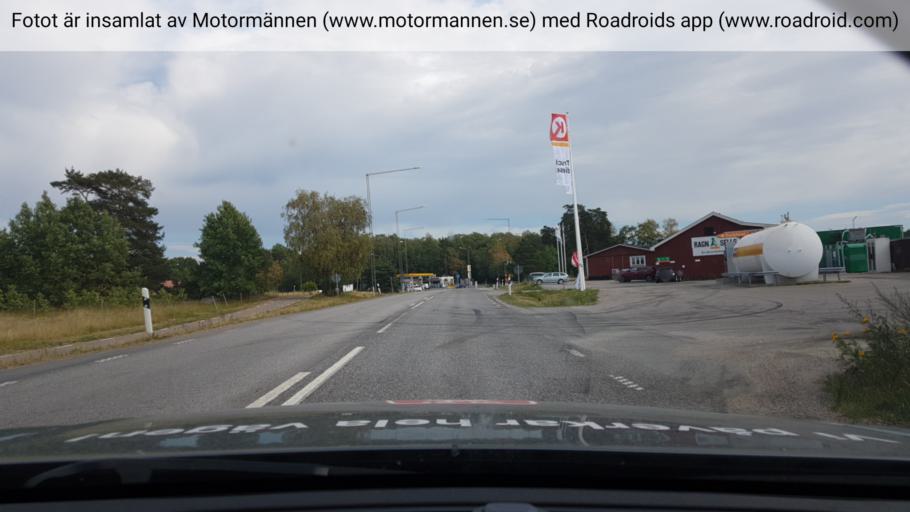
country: SE
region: Uppsala
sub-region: Uppsala Kommun
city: Uppsala
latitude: 59.8466
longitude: 17.5486
